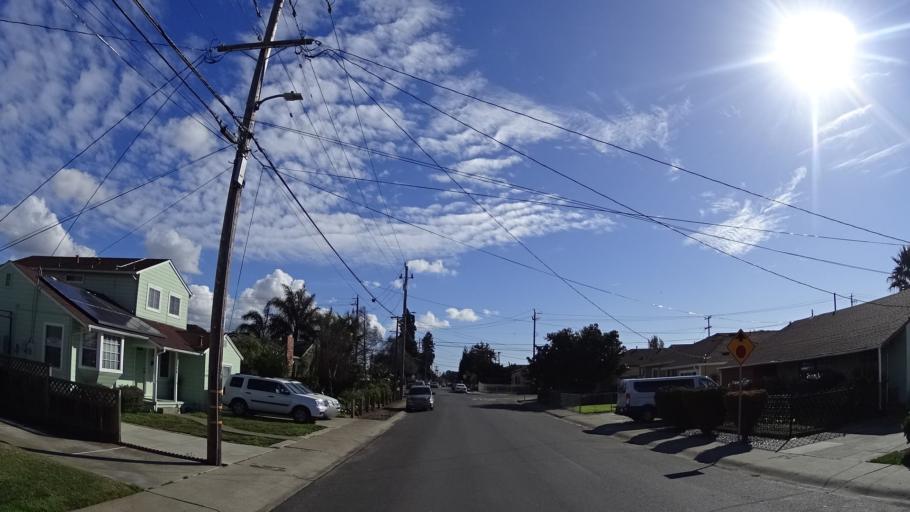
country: US
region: California
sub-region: Alameda County
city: San Lorenzo
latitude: 37.6709
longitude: -122.1163
